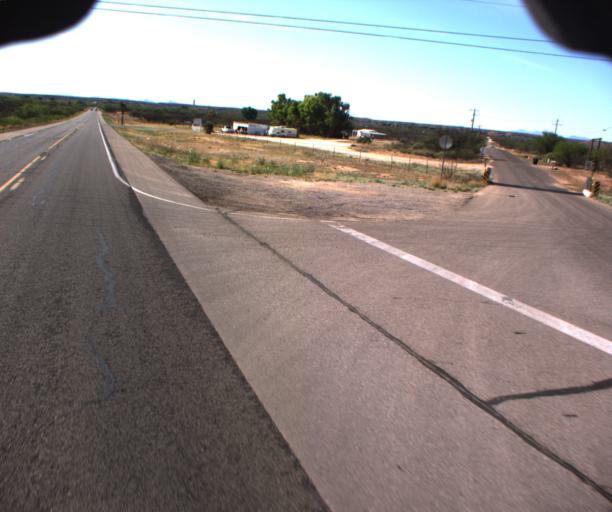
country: US
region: Arizona
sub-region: Cochise County
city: Saint David
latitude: 31.9179
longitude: -110.2646
